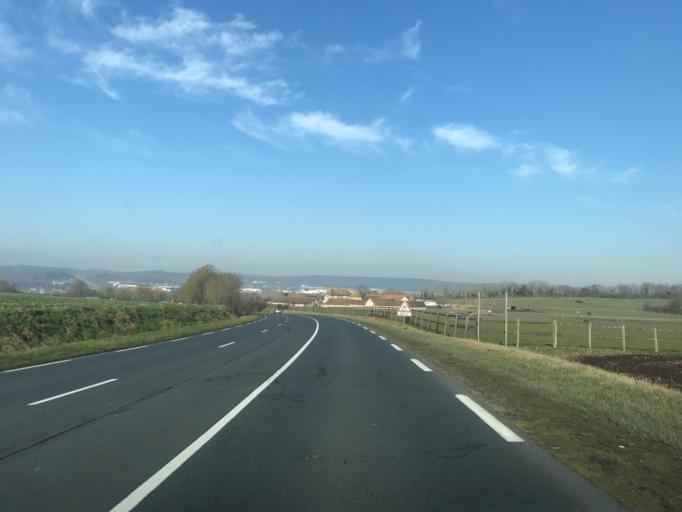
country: FR
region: Haute-Normandie
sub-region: Departement de l'Eure
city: Le Vaudreuil
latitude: 49.2378
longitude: 1.2023
